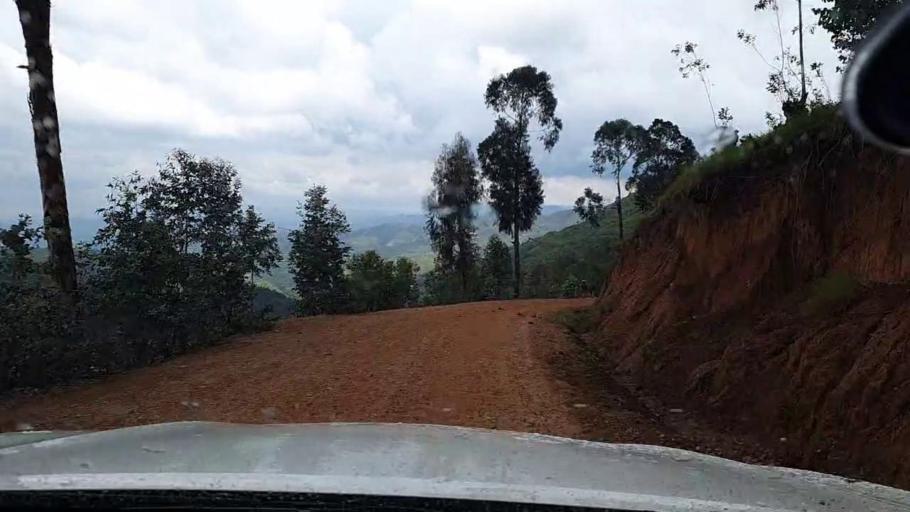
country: RW
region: Western Province
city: Kibuye
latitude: -2.1466
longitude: 29.4247
